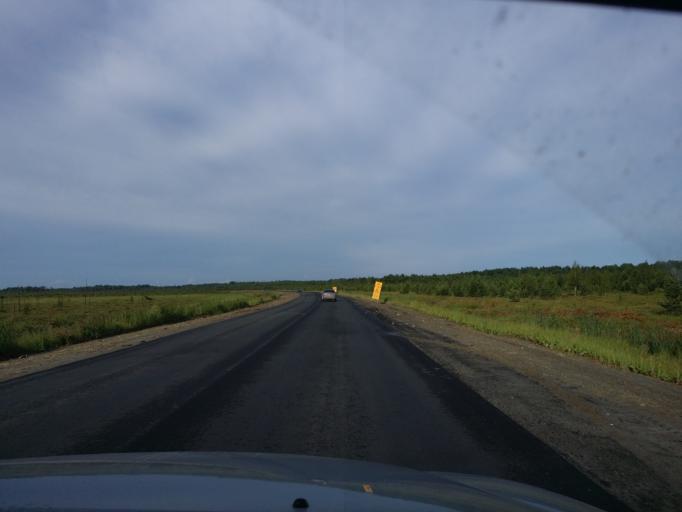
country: RU
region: Tjumen
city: Uvat
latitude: 59.3644
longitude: 68.9930
